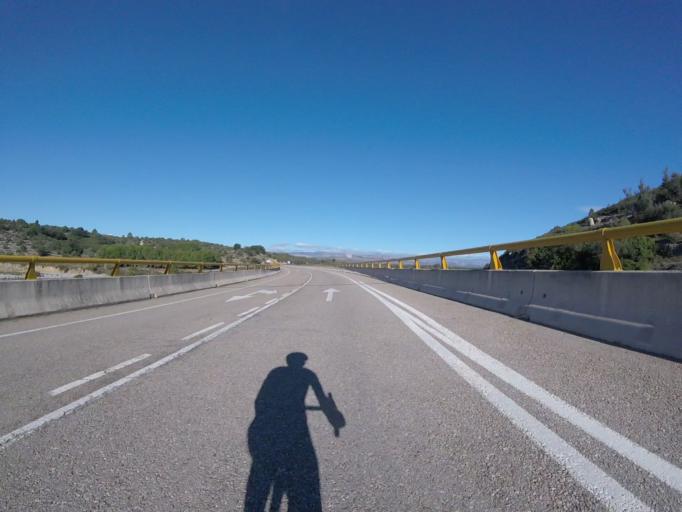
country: ES
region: Valencia
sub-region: Provincia de Castello
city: Cervera del Maestre
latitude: 40.4657
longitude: 0.2506
